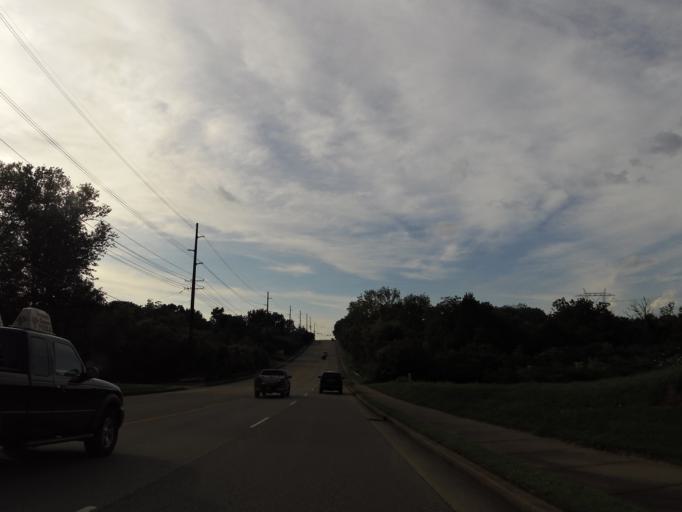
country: US
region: Tennessee
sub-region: Blount County
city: Louisville
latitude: 35.8998
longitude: -84.0728
